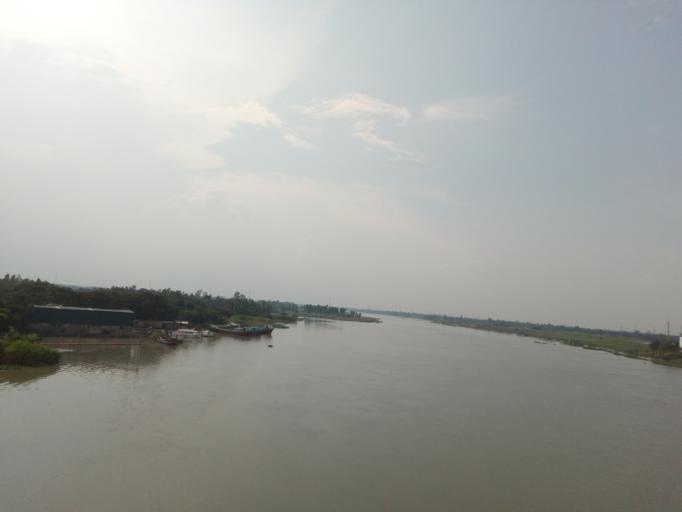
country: BD
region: Dhaka
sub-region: Dhaka
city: Dhaka
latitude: 23.6429
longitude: 90.3482
